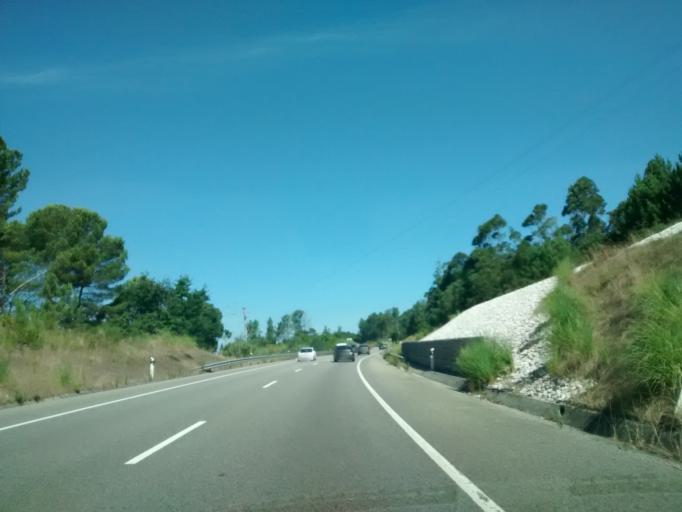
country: PT
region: Aveiro
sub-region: Oliveira do Bairro
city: Oliveira do Bairro
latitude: 40.5053
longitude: -8.4916
